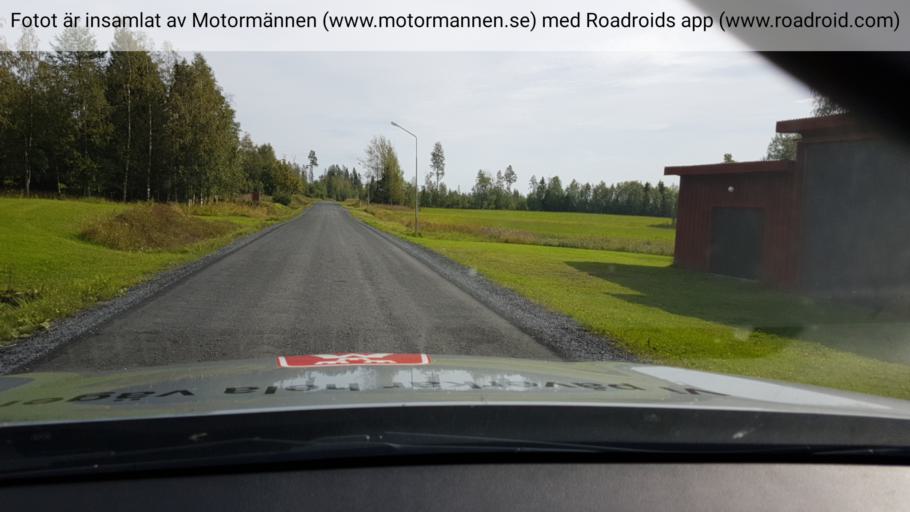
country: SE
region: Jaemtland
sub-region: Krokoms Kommun
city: Valla
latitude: 63.3501
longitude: 13.9908
